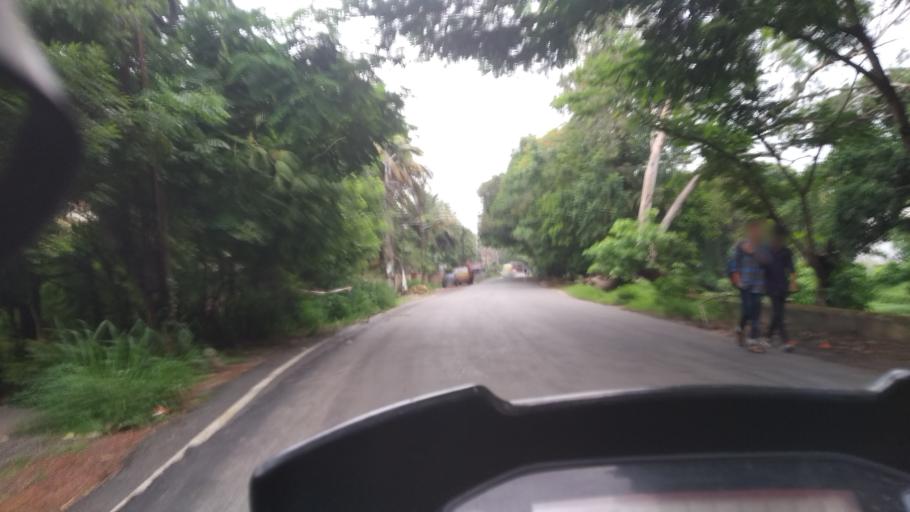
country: IN
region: Kerala
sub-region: Alappuzha
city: Alleppey
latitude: 9.4997
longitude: 76.3327
